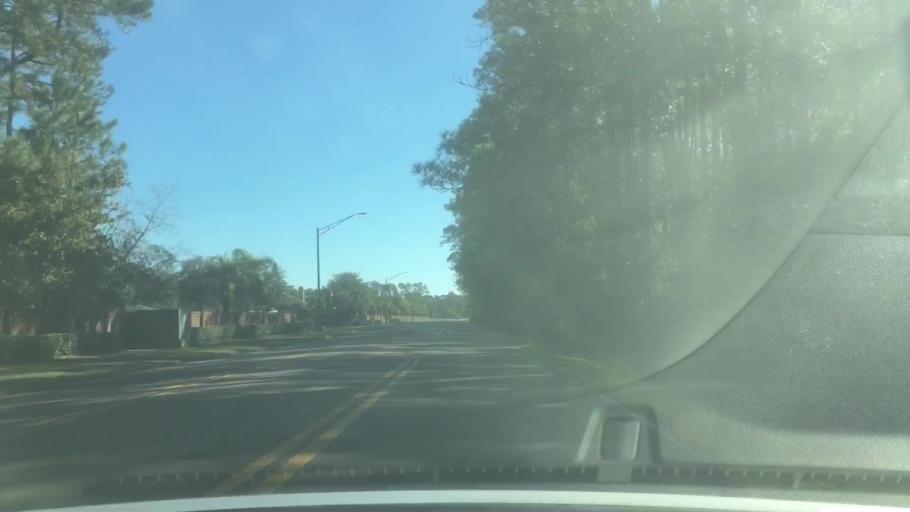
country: US
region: Florida
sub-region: Nassau County
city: Yulee
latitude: 30.4858
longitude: -81.6134
